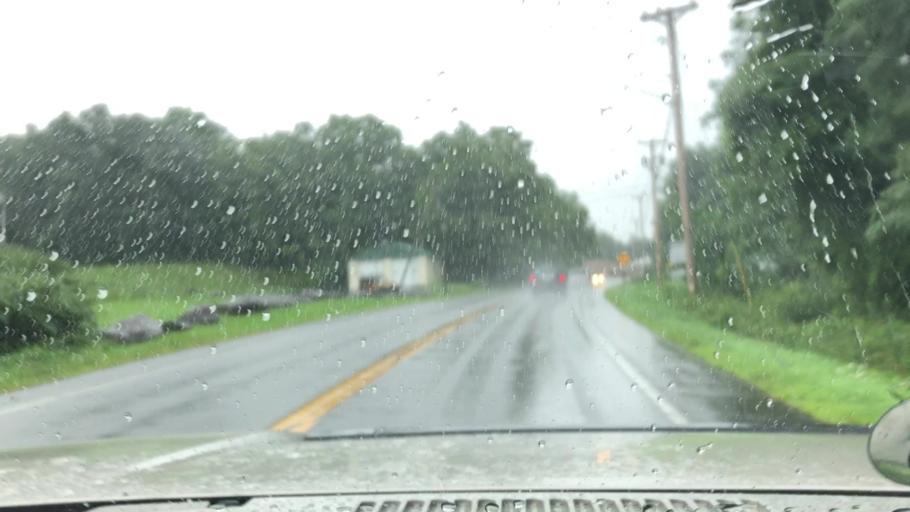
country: US
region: New York
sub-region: Greene County
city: Cairo
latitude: 42.2424
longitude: -73.9801
